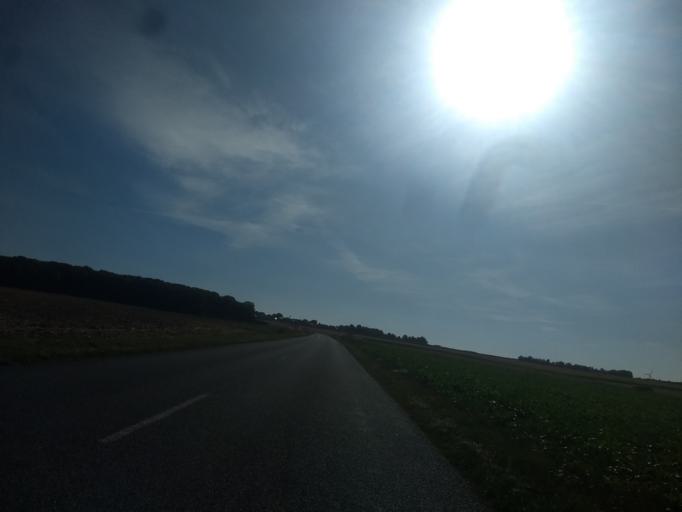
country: FR
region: Nord-Pas-de-Calais
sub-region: Departement du Pas-de-Calais
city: Roeux
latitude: 50.2801
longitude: 2.8967
